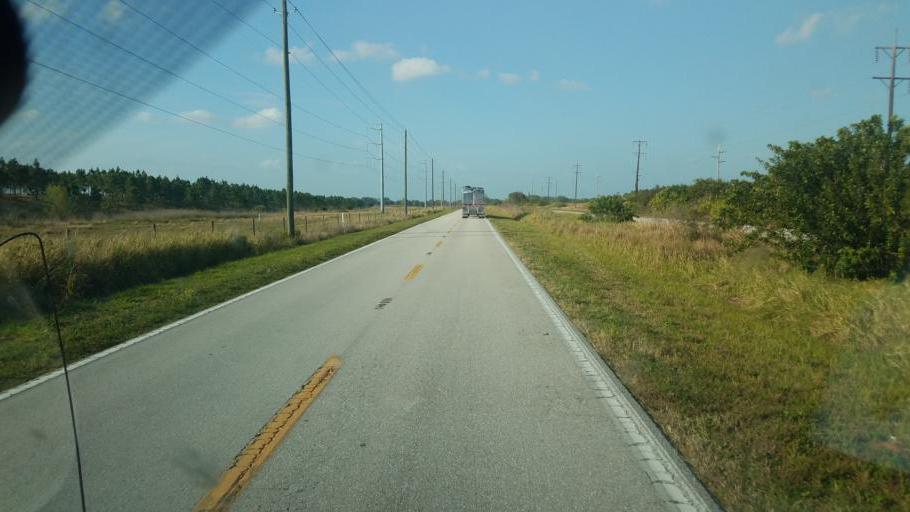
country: US
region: Florida
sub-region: Hardee County
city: Bowling Green
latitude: 27.7096
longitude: -81.9601
